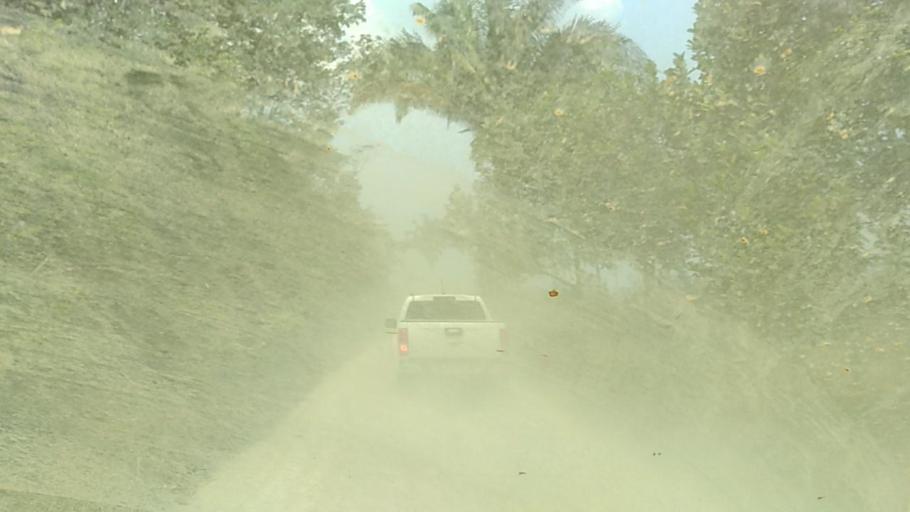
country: BR
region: Rondonia
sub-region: Porto Velho
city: Porto Velho
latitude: -8.7730
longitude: -63.2239
